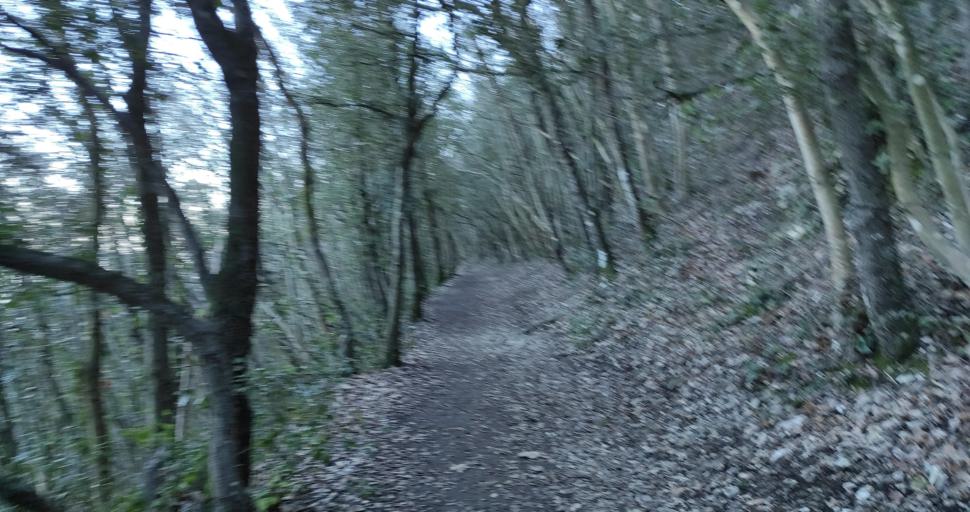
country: IT
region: The Marches
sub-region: Provincia di Ancona
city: Sirolo
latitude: 43.5469
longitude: 13.6192
